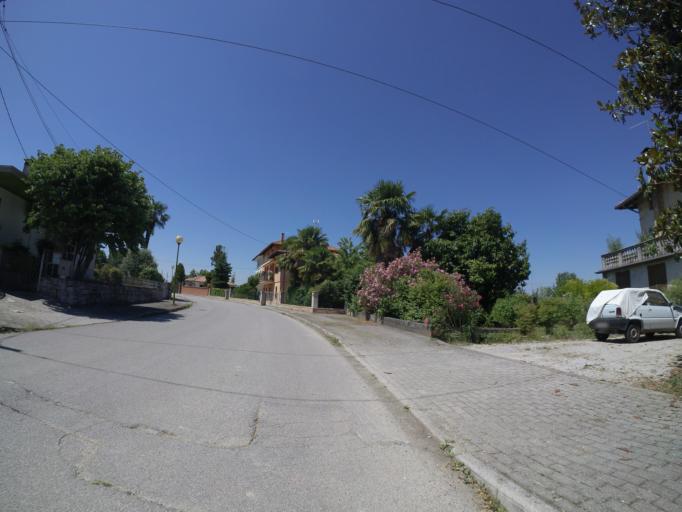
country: IT
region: Friuli Venezia Giulia
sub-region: Provincia di Udine
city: Teor
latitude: 45.8496
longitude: 13.0376
